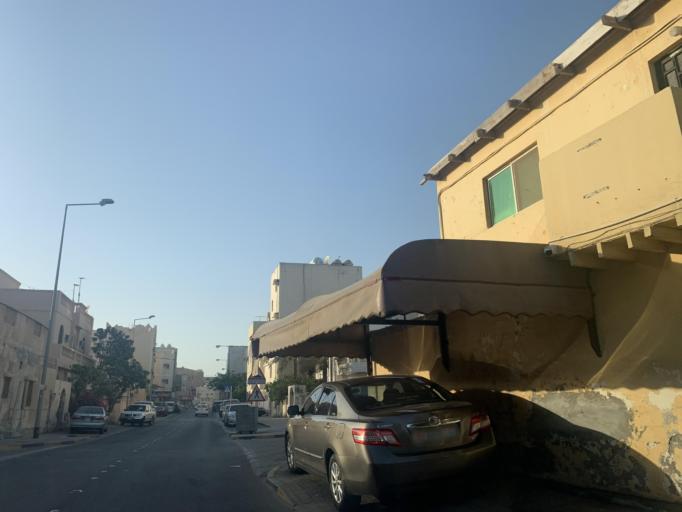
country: BH
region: Manama
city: Jidd Hafs
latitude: 26.2056
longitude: 50.4521
